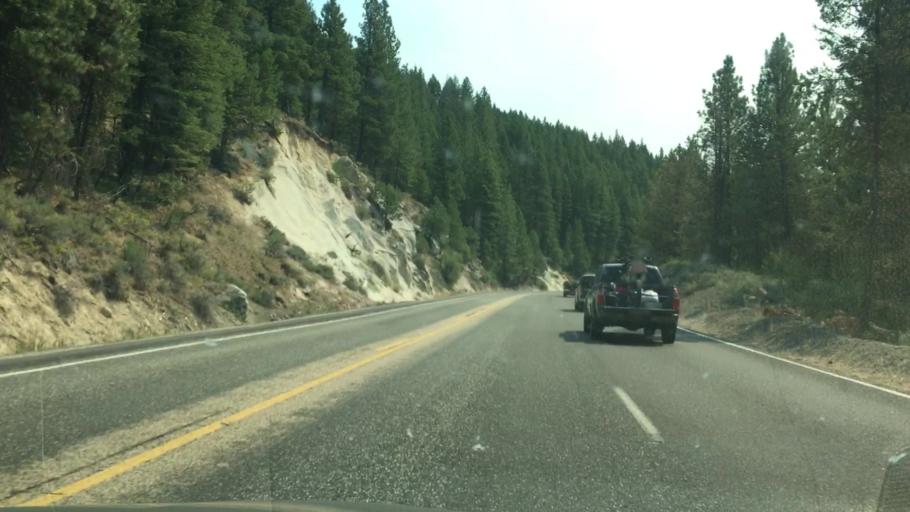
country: US
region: Idaho
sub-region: Valley County
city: Cascade
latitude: 44.5864
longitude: -116.0385
